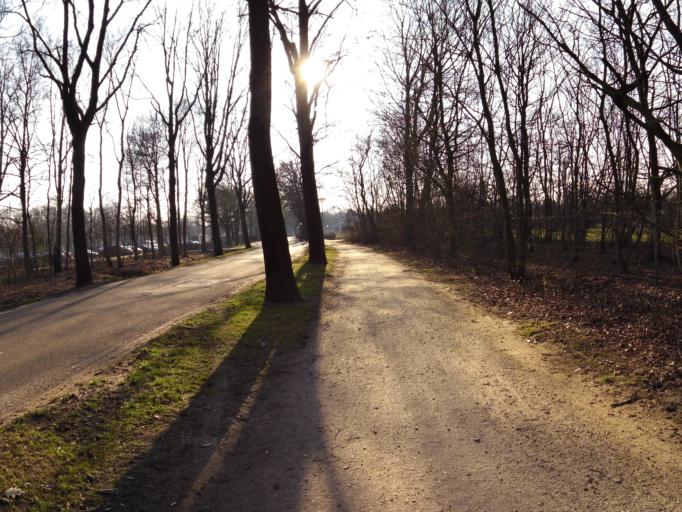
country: NL
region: North Brabant
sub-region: Gemeente Maasdonk
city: Geffen
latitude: 51.7052
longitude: 5.4316
